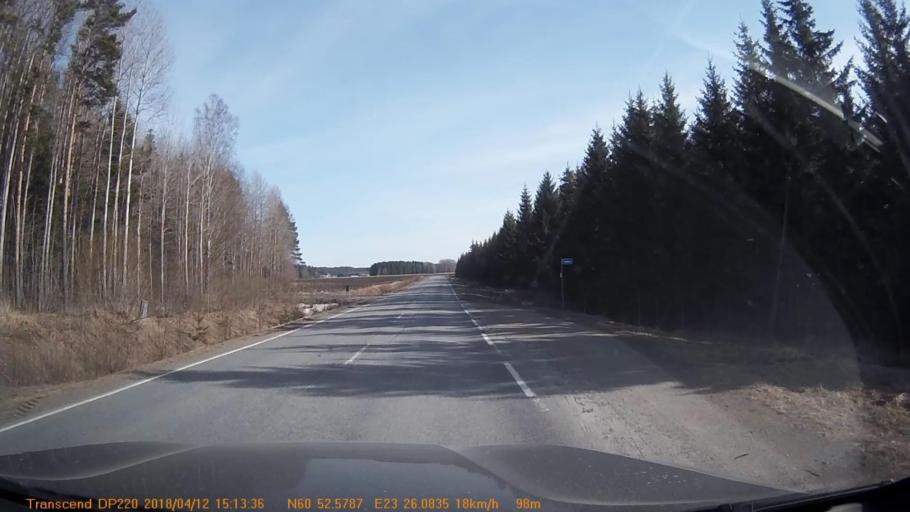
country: FI
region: Haeme
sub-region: Forssa
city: Jokioinen
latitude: 60.8764
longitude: 23.4346
